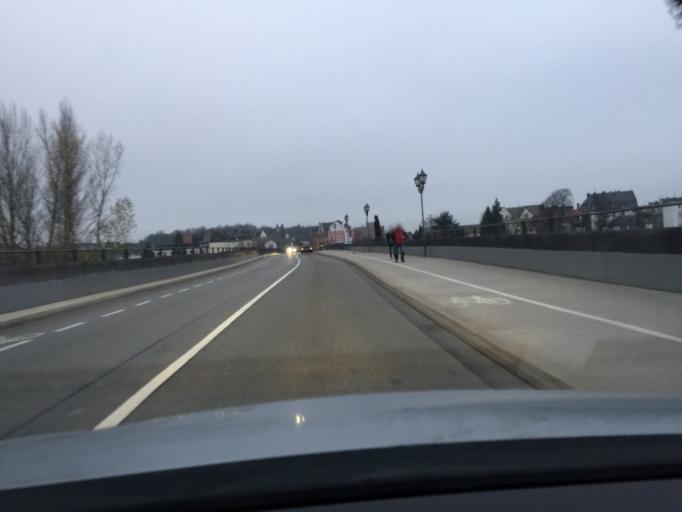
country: DE
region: Rheinland-Pfalz
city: Koblenz
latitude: 50.3633
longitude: 7.5932
